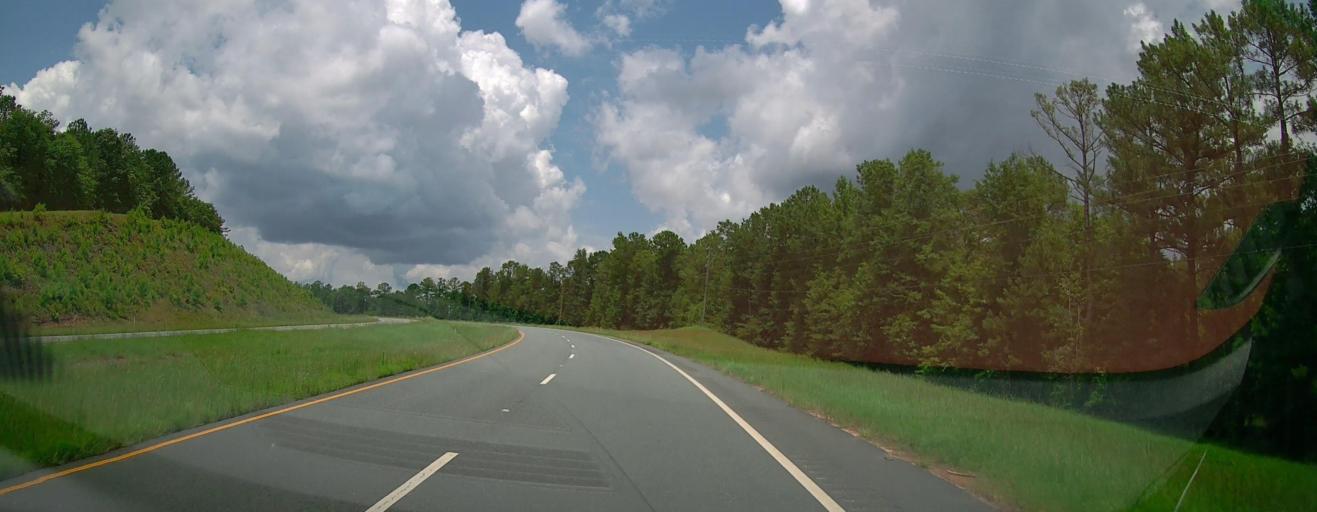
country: US
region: Georgia
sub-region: Upson County
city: Thomaston
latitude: 32.8150
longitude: -84.2870
